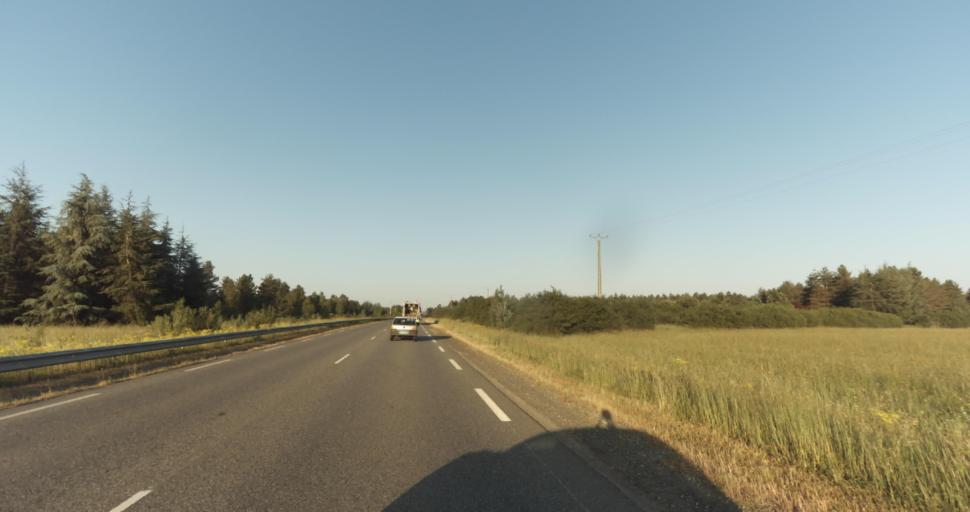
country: FR
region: Midi-Pyrenees
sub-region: Departement de la Haute-Garonne
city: Fontenilles
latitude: 43.5735
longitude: 1.2061
